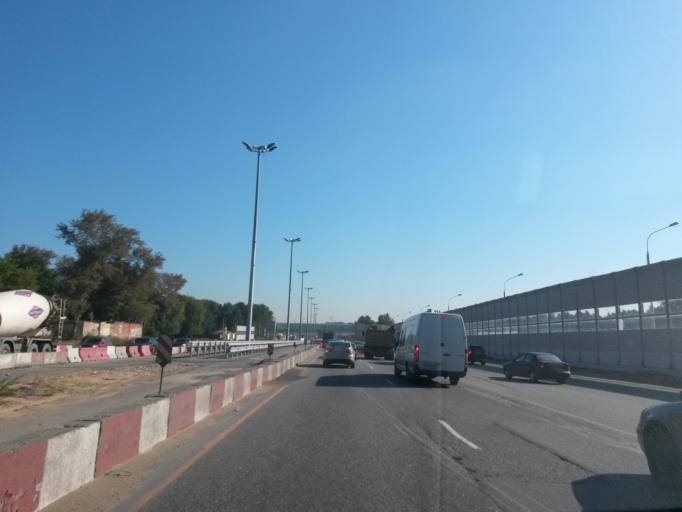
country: RU
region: Moskovskaya
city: Bolshevo
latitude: 55.9323
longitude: 37.8059
